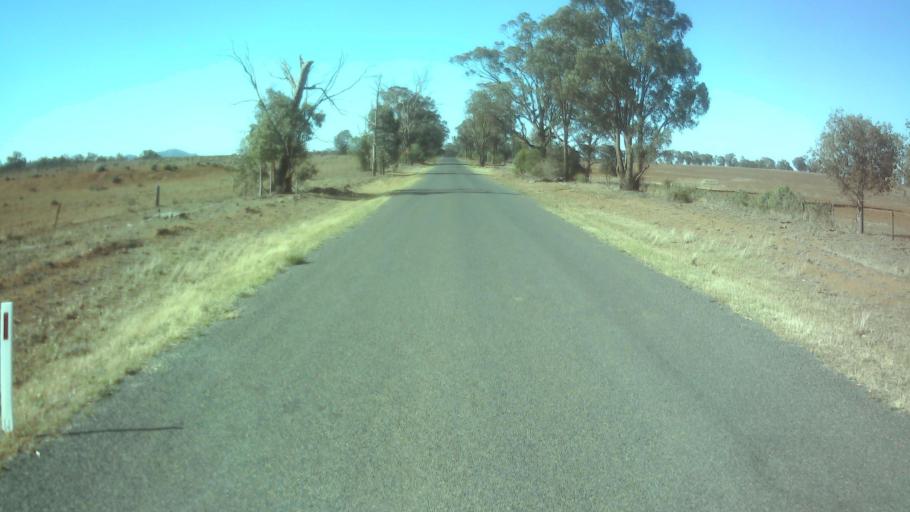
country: AU
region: New South Wales
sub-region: Forbes
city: Forbes
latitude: -33.7013
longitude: 147.8065
